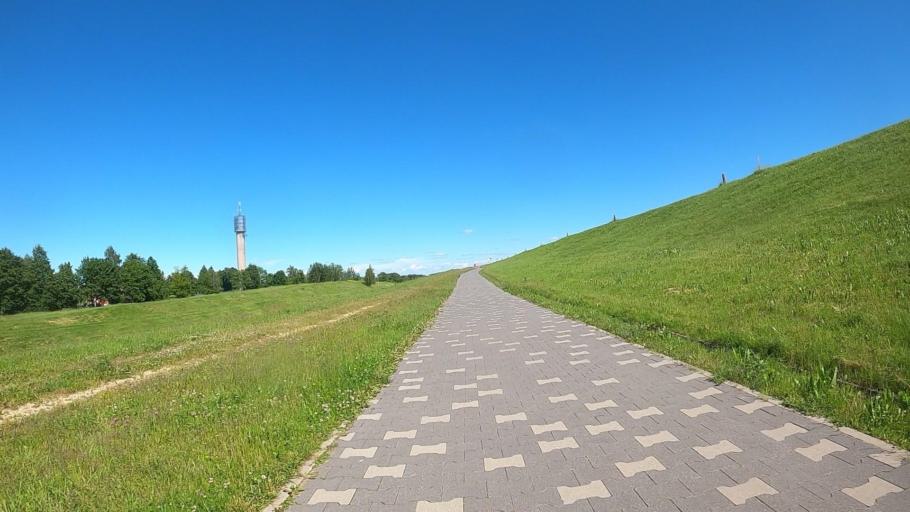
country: LV
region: Salaspils
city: Salaspils
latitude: 56.8485
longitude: 24.3365
